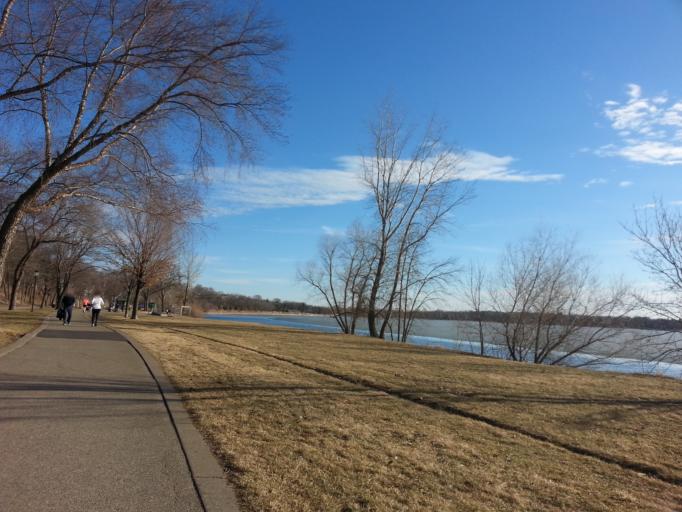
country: US
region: Minnesota
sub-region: Hennepin County
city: Saint Louis Park
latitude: 44.9458
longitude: -93.3055
